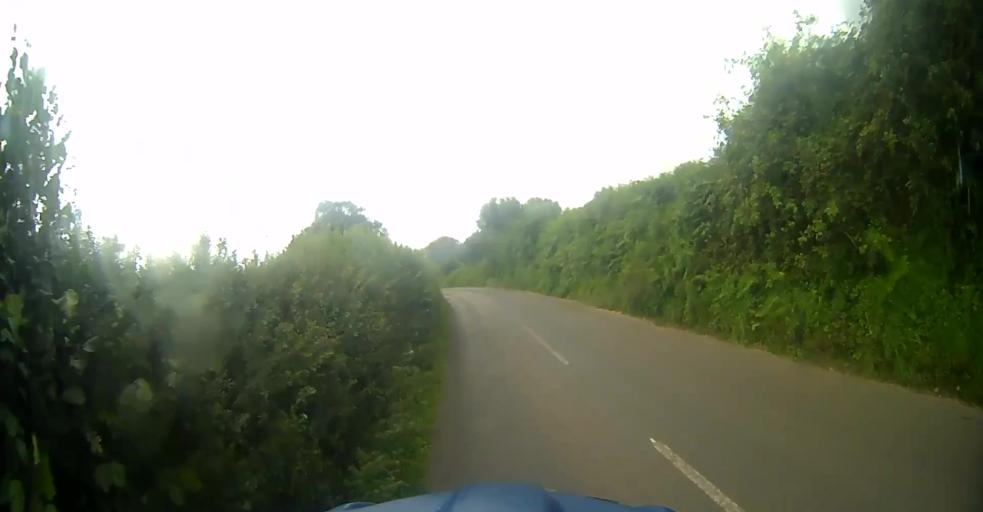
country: GB
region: England
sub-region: Hampshire
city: Alton
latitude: 51.1857
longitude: -1.0184
